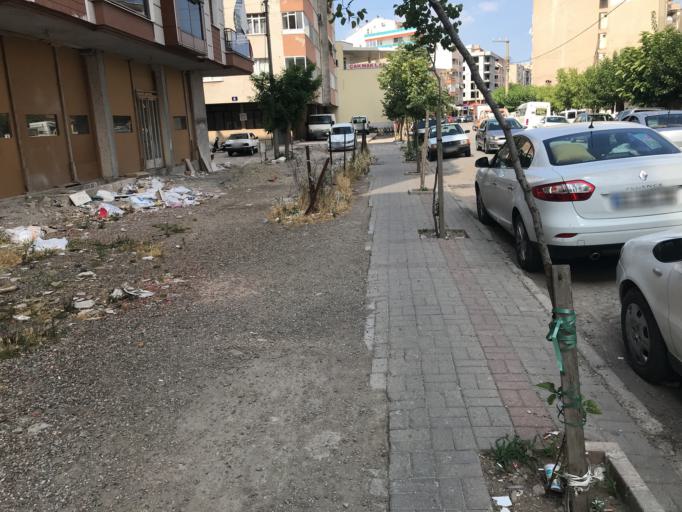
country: TR
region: Izmir
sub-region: Bergama
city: Bergama
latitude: 39.1138
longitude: 27.1802
